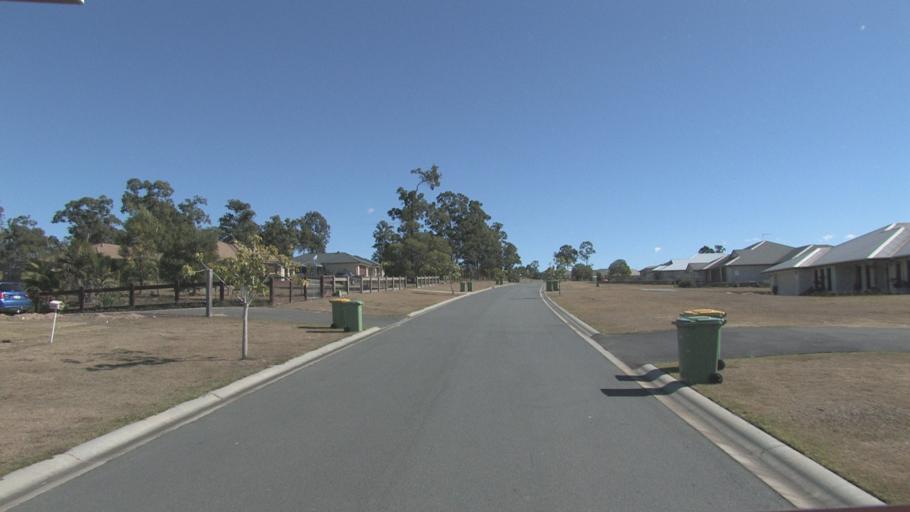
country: AU
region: Queensland
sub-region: Logan
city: North Maclean
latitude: -27.7551
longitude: 152.9488
